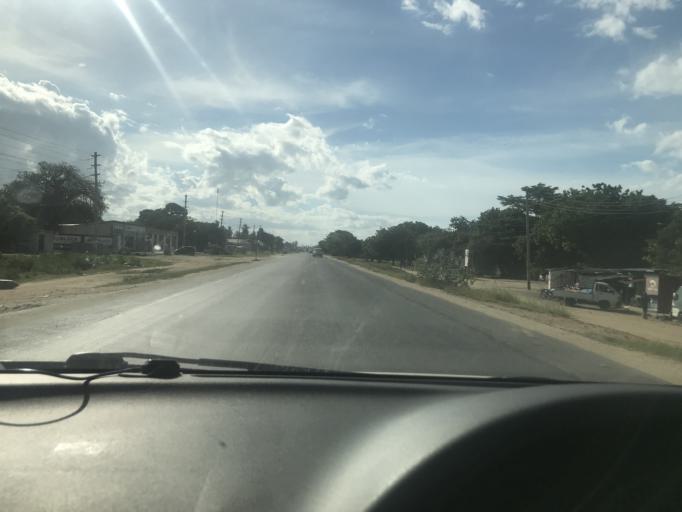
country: TZ
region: Dar es Salaam
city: Magomeni
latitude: -6.6456
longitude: 39.1691
